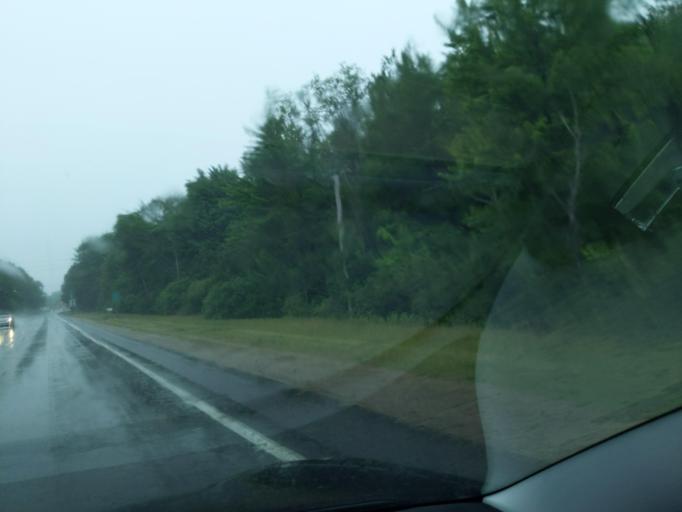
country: US
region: Michigan
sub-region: Muskegon County
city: Fruitport
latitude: 43.1521
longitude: -86.1715
